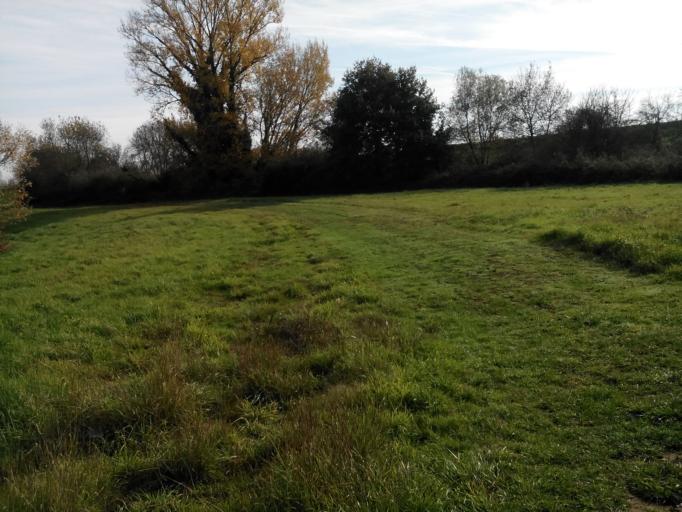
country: FR
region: Centre
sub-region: Departement d'Indre-et-Loire
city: Fondettes
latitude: 47.3794
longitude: 0.6067
